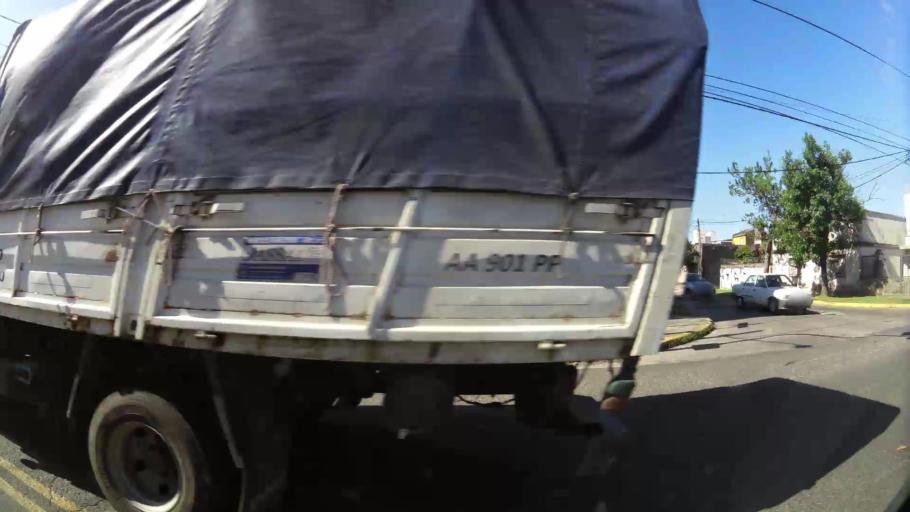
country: AR
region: Santa Fe
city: Santa Fe de la Vera Cruz
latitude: -31.6198
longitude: -60.6903
